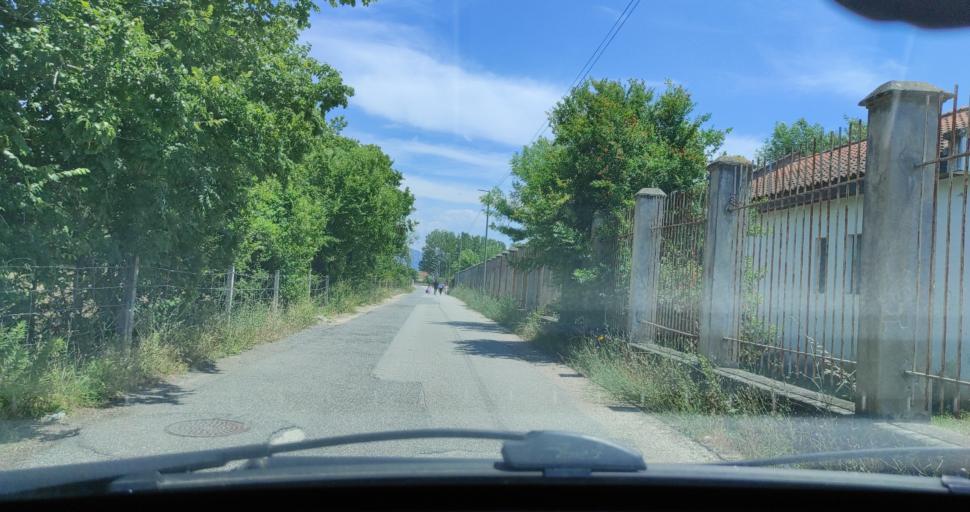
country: AL
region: Shkoder
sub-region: Rrethi i Shkodres
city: Velipoje
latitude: 41.8731
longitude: 19.4006
